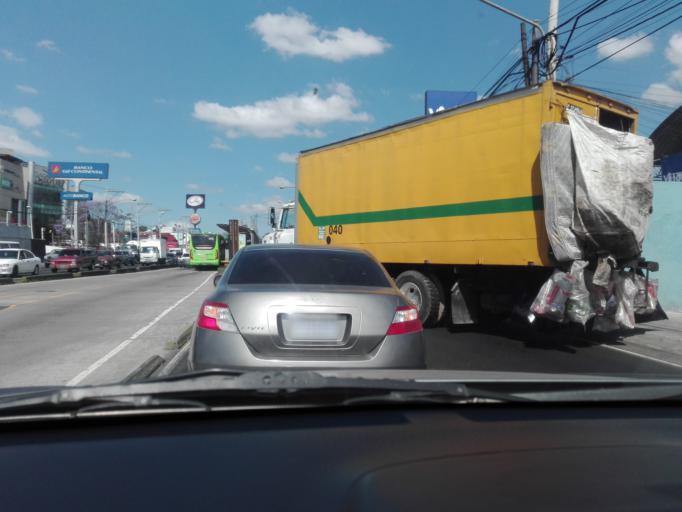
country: GT
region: Guatemala
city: Mixco
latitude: 14.5922
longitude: -90.5592
